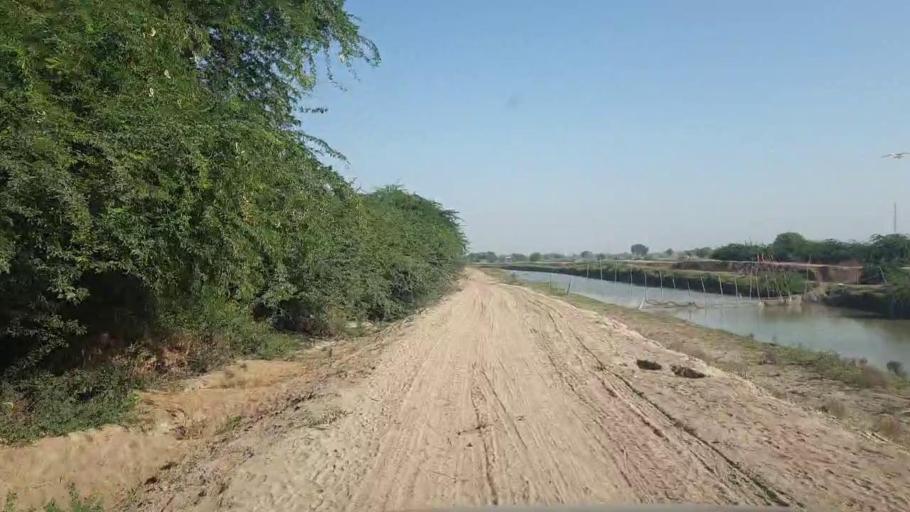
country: PK
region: Sindh
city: Badin
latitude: 24.7255
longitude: 68.8036
